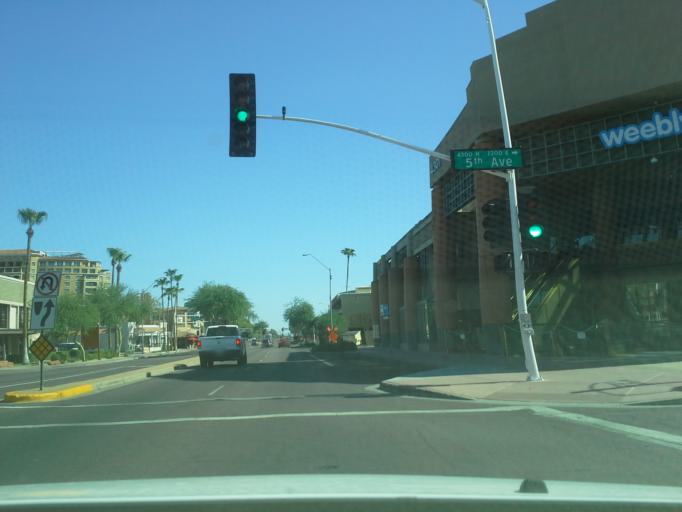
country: US
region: Arizona
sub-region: Maricopa County
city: Scottsdale
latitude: 33.4983
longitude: -111.9260
